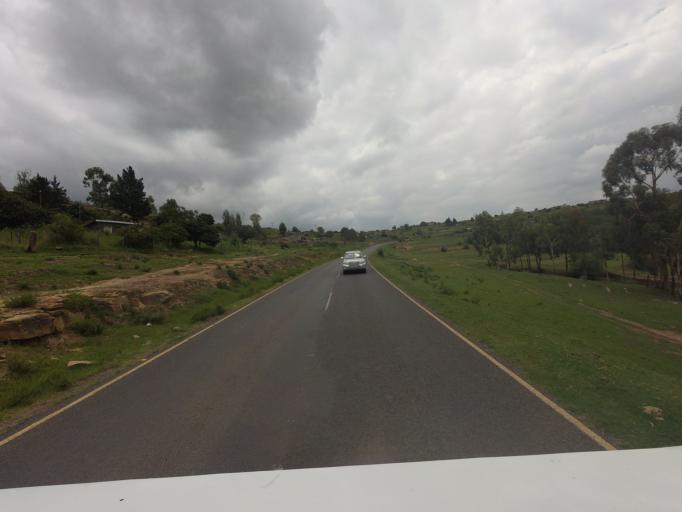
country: LS
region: Leribe
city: Leribe
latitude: -28.8905
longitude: 28.1039
